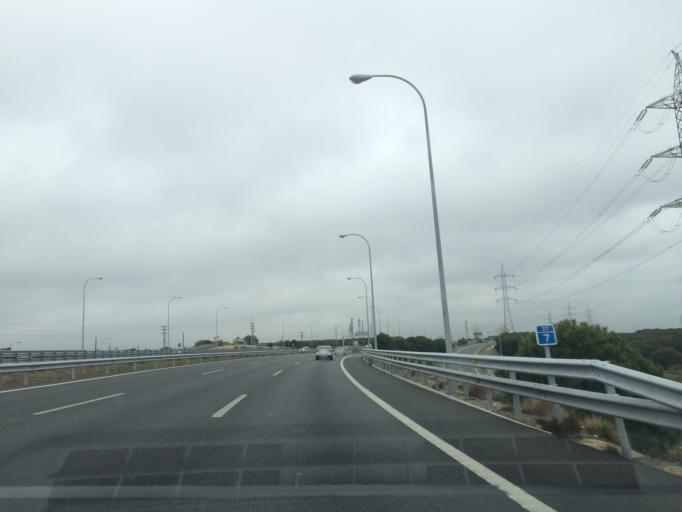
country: ES
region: Madrid
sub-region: Provincia de Madrid
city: Pozuelo de Alarcon
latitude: 40.4058
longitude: -3.8287
